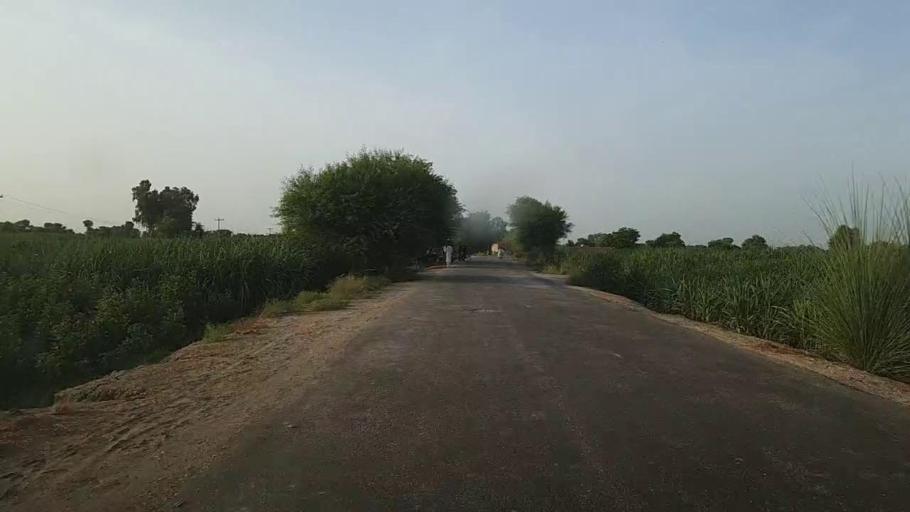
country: PK
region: Sindh
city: Ubauro
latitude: 28.1754
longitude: 69.8291
